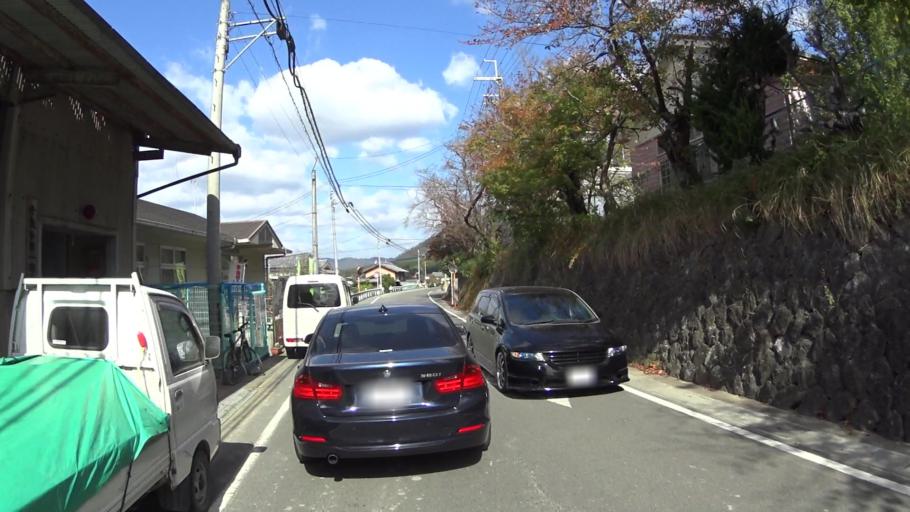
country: JP
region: Kyoto
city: Kameoka
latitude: 35.0523
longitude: 135.5797
